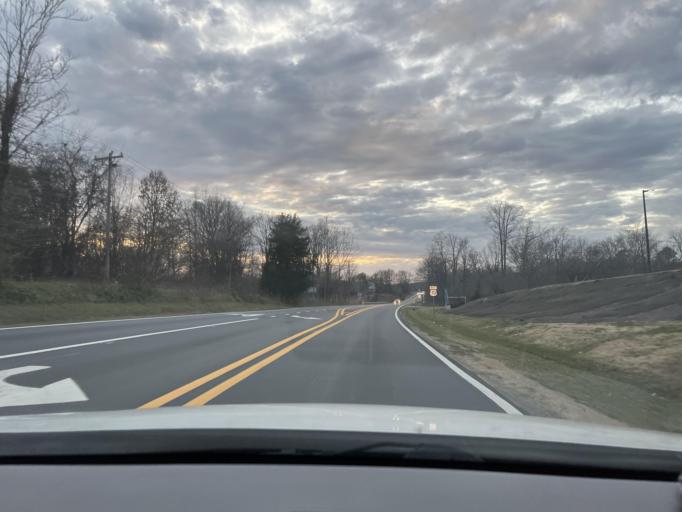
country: US
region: North Carolina
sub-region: Guilford County
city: Gibsonville
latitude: 36.0794
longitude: -79.5447
